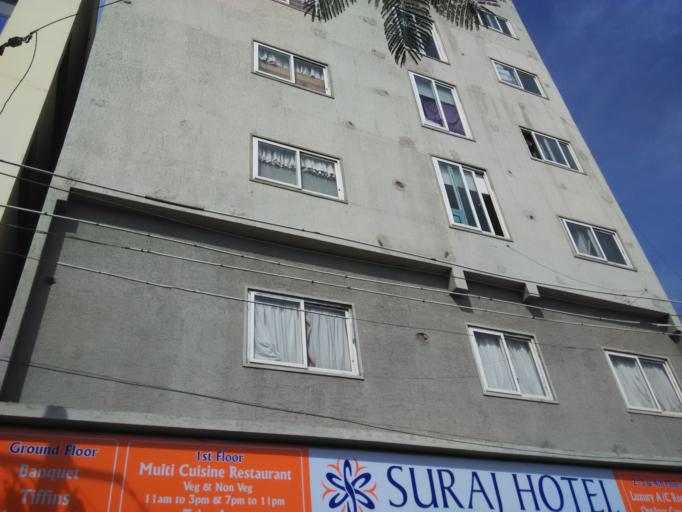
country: IN
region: Andhra Pradesh
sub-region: Kurnool
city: Nandyal
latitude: 15.4865
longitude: 78.4771
